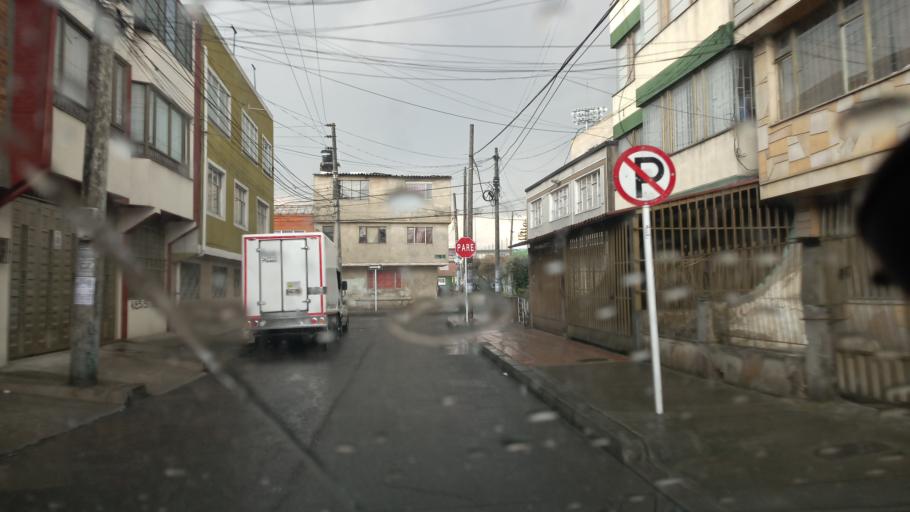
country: CO
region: Cundinamarca
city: Funza
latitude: 4.6720
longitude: -74.1410
